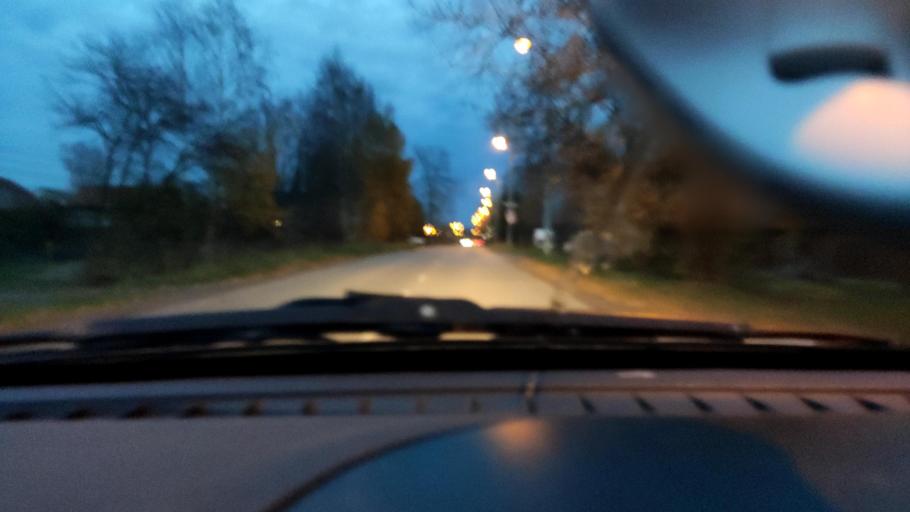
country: RU
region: Perm
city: Perm
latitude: 57.9779
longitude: 56.2997
